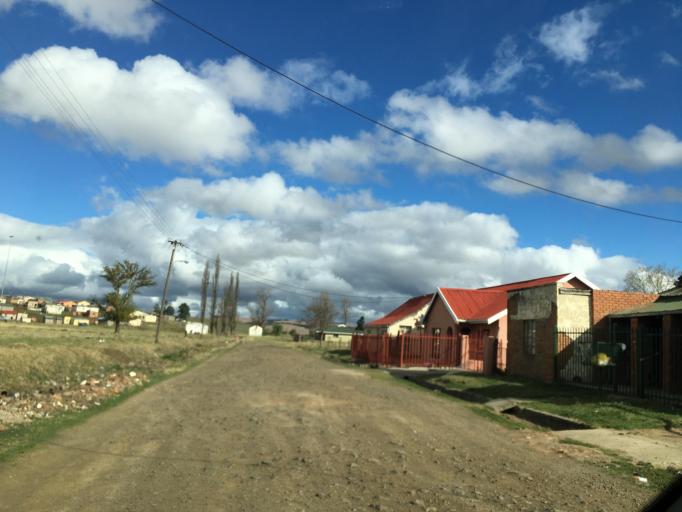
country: ZA
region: Eastern Cape
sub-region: Chris Hani District Municipality
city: Elliot
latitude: -31.3345
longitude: 27.8524
